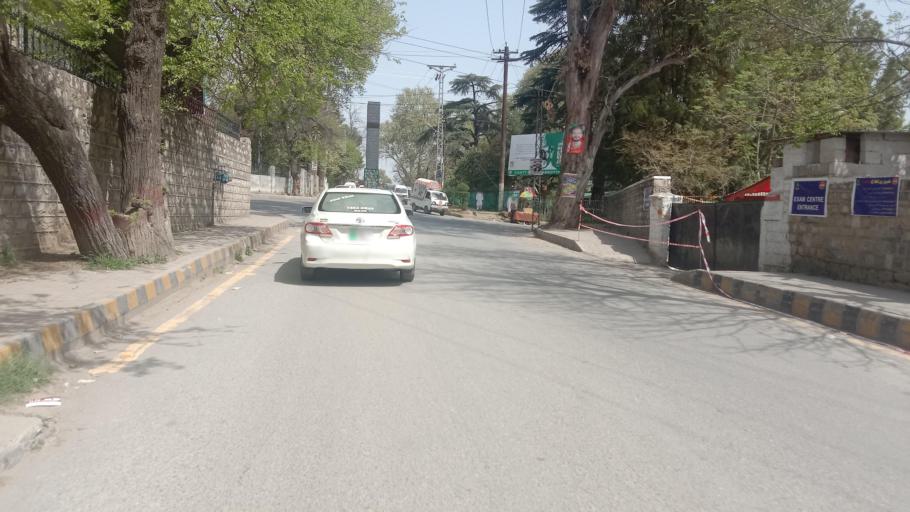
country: PK
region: Khyber Pakhtunkhwa
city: Abbottabad
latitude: 34.1487
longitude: 73.2135
